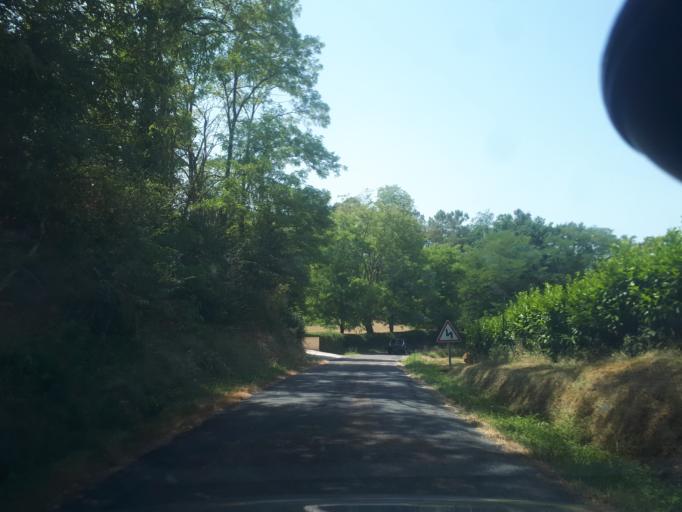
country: FR
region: Midi-Pyrenees
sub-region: Departement du Lot
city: Gourdon
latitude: 44.7519
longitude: 1.3406
